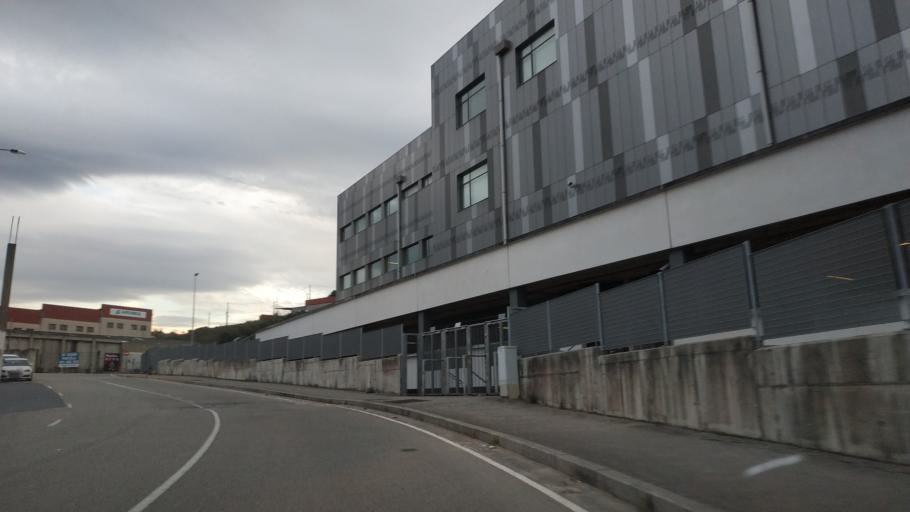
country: ES
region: Galicia
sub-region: Provincia da Coruna
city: A Coruna
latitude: 43.3441
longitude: -8.4264
